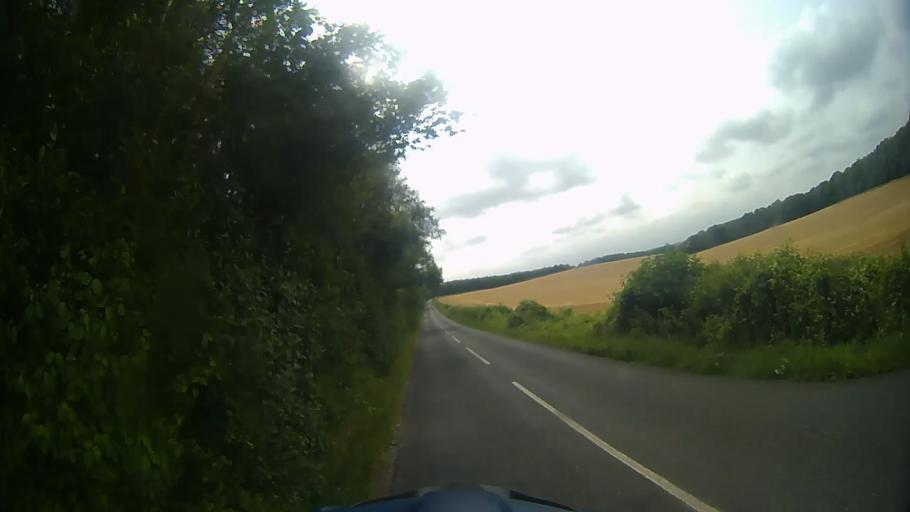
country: GB
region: England
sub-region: Hampshire
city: Overton
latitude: 51.2832
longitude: -1.2826
